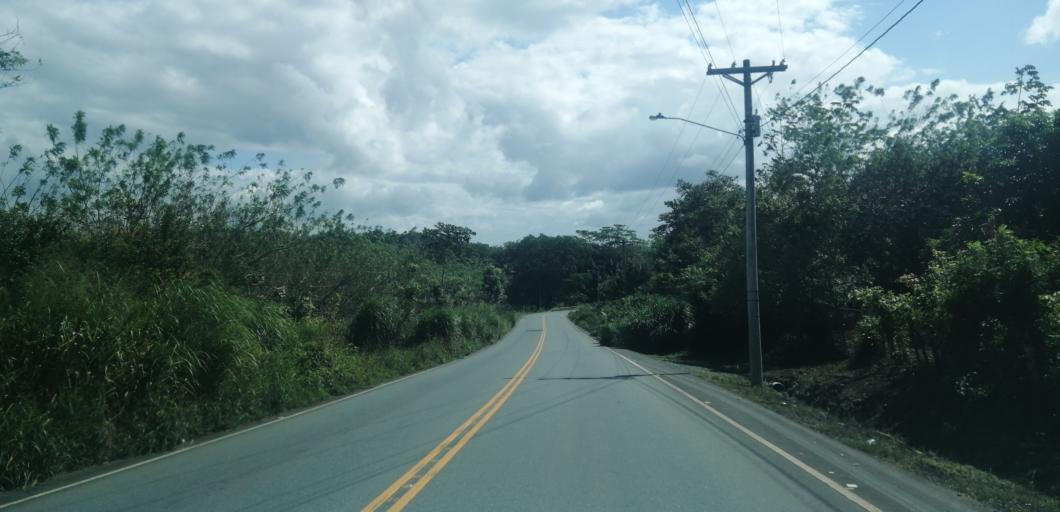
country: PA
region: Panama
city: Canita
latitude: 9.2213
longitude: -78.9202
